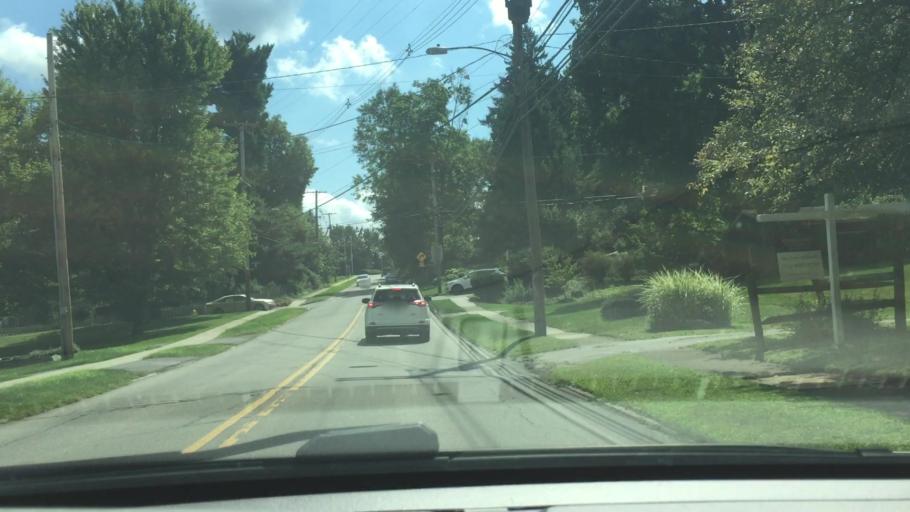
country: US
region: Pennsylvania
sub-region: Lawrence County
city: New Wilmington
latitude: 41.1171
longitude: -80.3354
